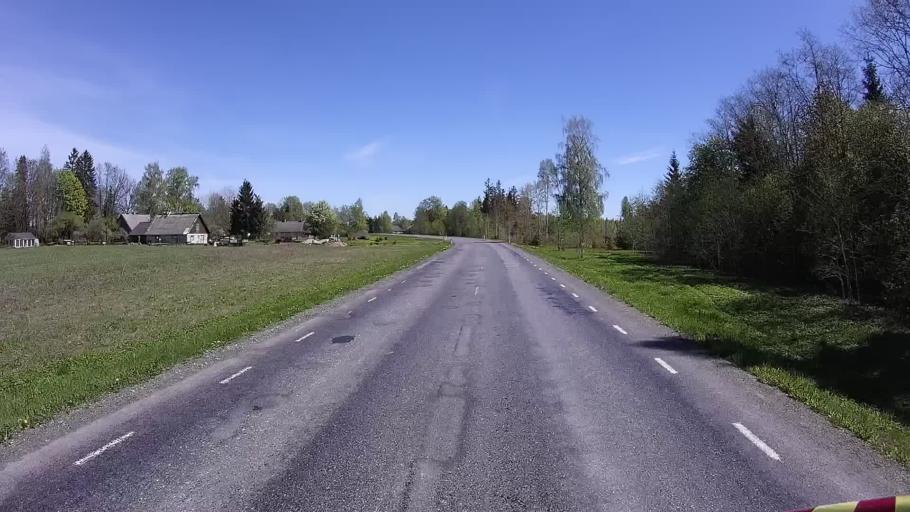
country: EE
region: Raplamaa
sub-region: Kehtna vald
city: Kehtna
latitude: 59.0541
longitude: 24.9638
